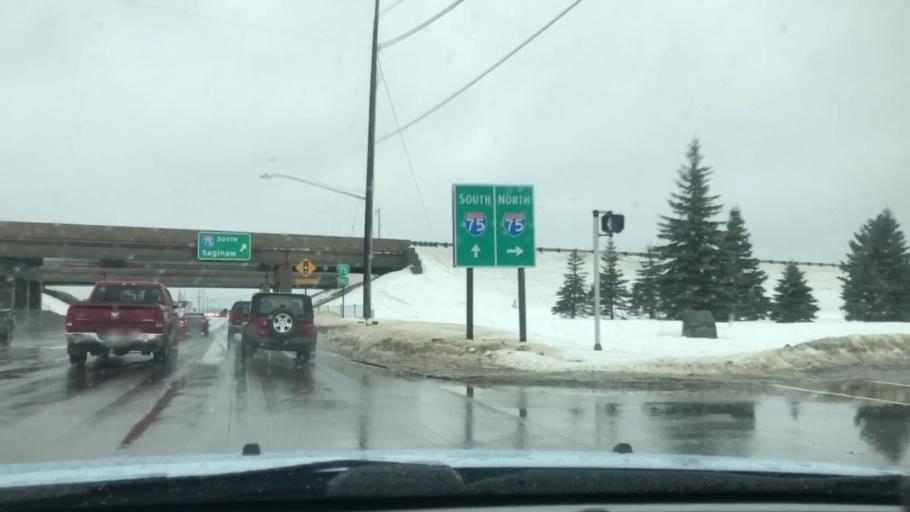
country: US
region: Michigan
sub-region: Otsego County
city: Gaylord
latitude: 45.0275
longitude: -84.6867
